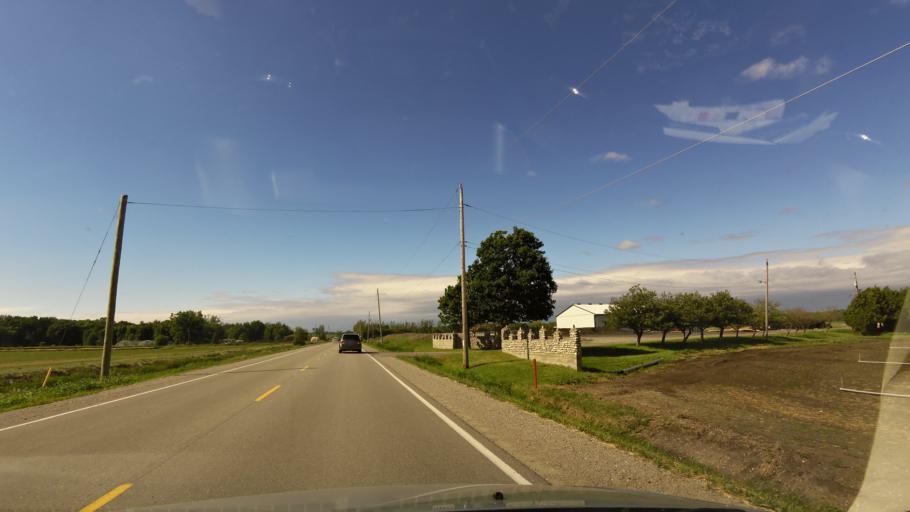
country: CA
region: Ontario
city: Innisfil
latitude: 44.2284
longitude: -79.6340
